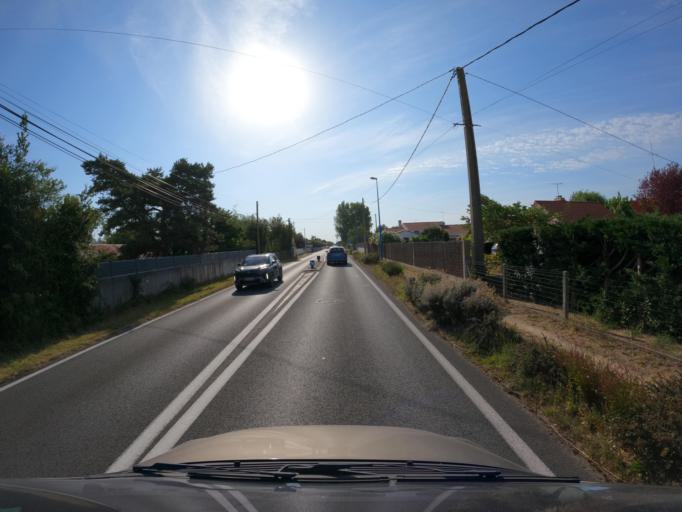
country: FR
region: Pays de la Loire
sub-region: Departement de la Vendee
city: Saint-Jean-de-Monts
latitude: 46.8034
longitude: -2.0890
